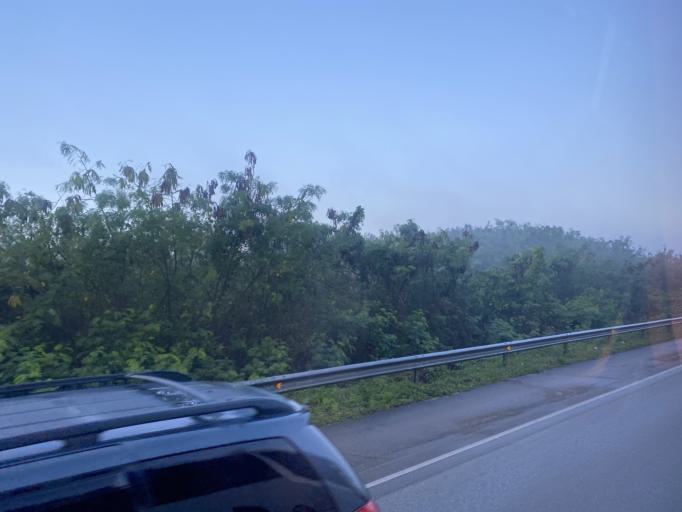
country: DO
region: La Altagracia
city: Otra Banda
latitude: 18.7332
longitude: -68.5064
